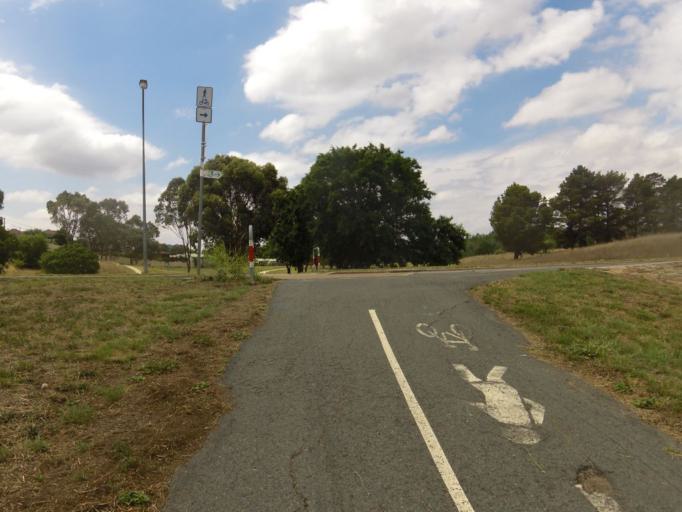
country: AU
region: Australian Capital Territory
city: Macarthur
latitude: -35.4208
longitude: 149.0890
